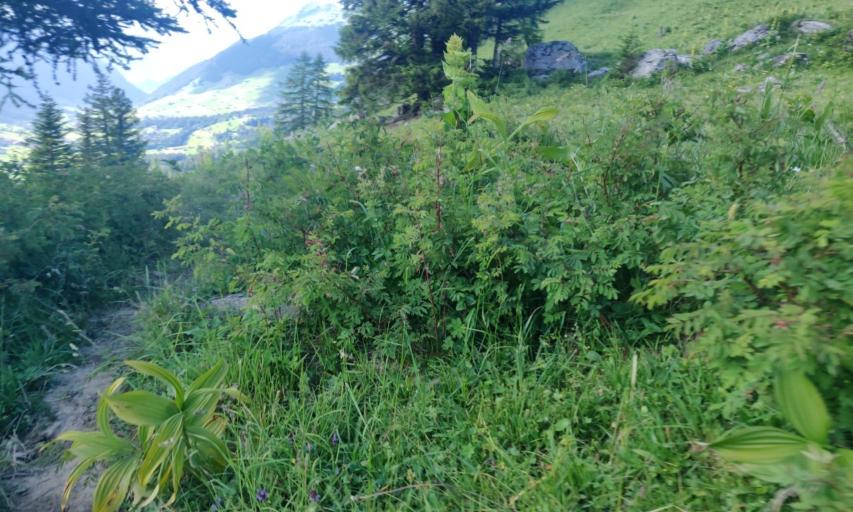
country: CH
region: Bern
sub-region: Obersimmental-Saanen District
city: Gstaad
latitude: 46.3905
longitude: 7.3471
